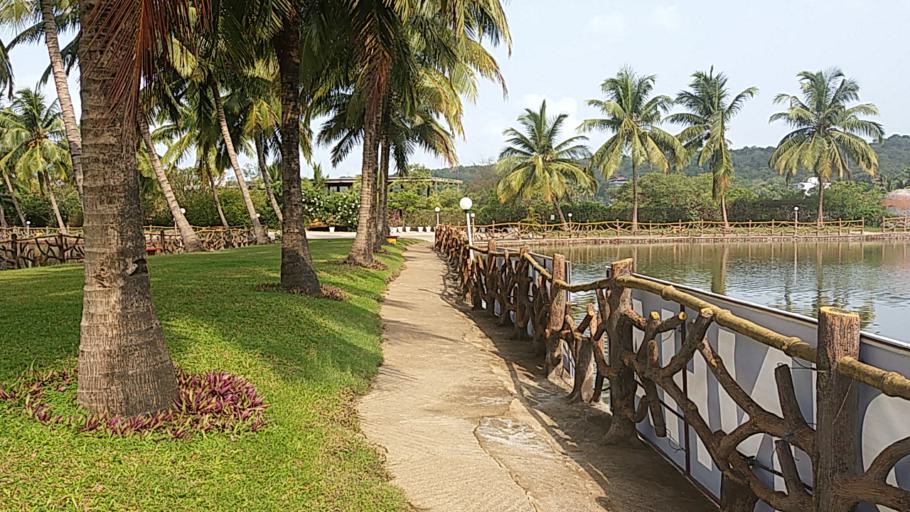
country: IN
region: Goa
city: Calangute
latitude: 15.5673
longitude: 73.7598
